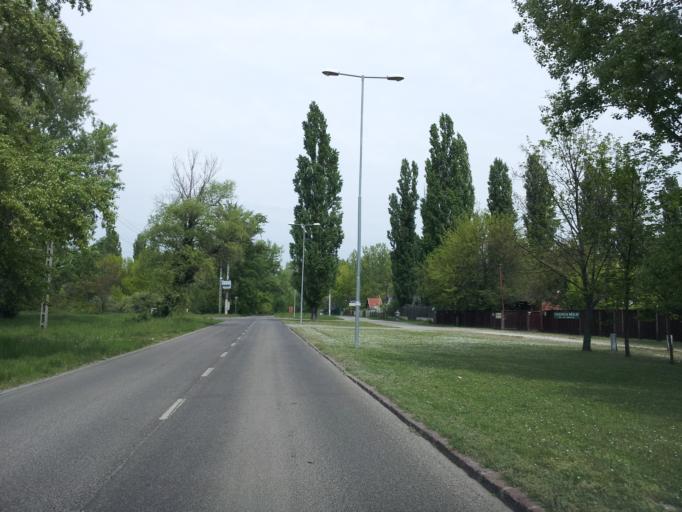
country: HU
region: Pest
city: Budakalasz
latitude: 47.6033
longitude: 19.0686
